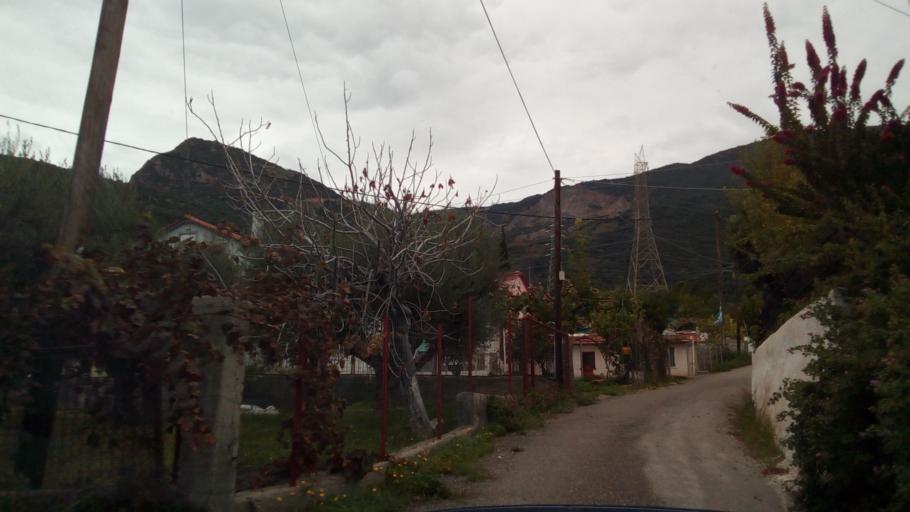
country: GR
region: West Greece
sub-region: Nomos Achaias
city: Kamarai
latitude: 38.3950
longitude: 22.0161
